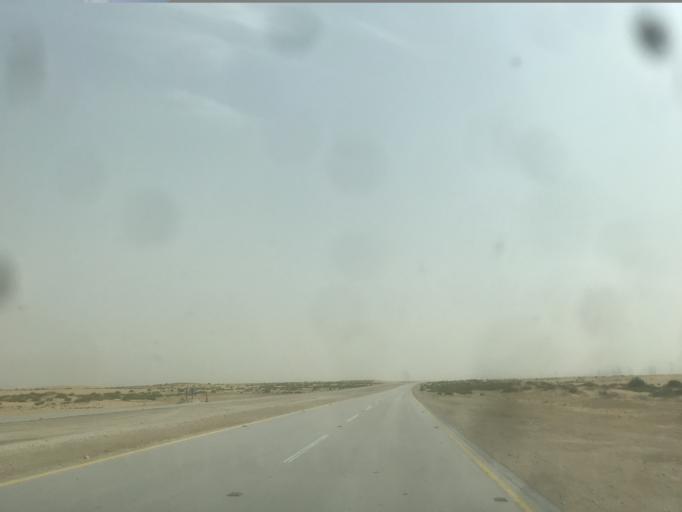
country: SA
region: Eastern Province
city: Abqaiq
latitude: 25.9173
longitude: 49.8548
